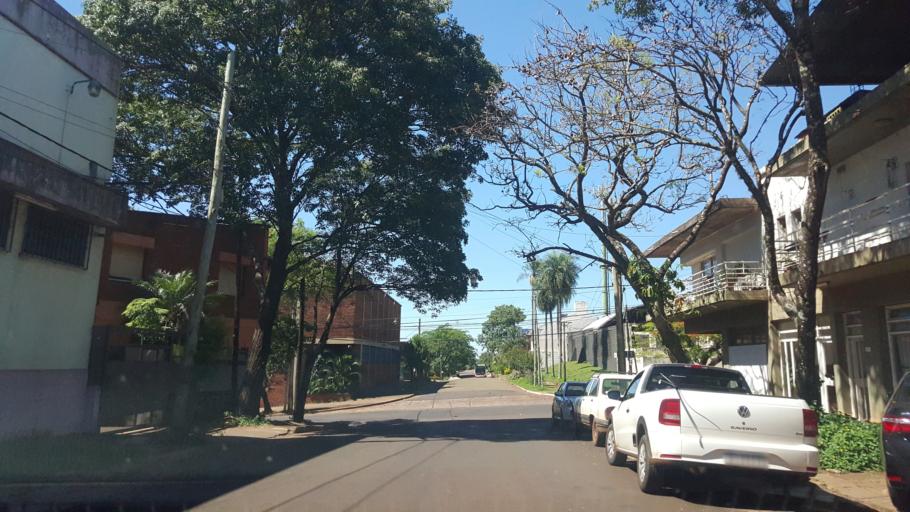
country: AR
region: Misiones
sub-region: Departamento de Capital
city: Posadas
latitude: -27.3938
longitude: -55.9024
